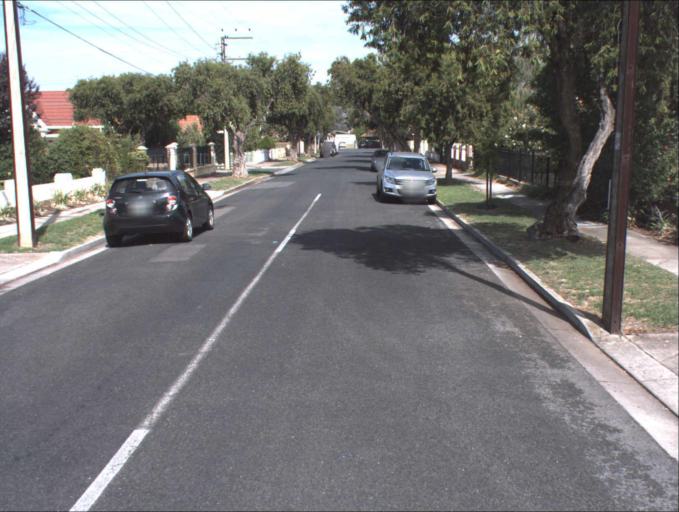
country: AU
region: South Australia
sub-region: Port Adelaide Enfield
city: Klemzig
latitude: -34.8790
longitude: 138.6213
